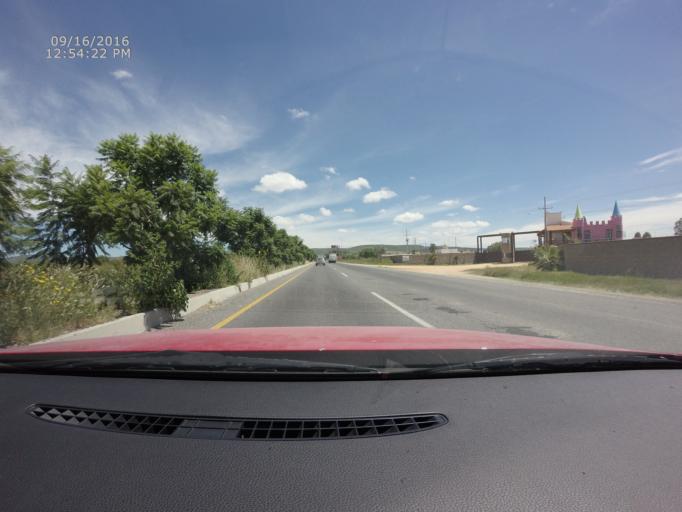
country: MX
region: Queretaro
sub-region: Colon
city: Purisima de Cubos (La Purisima)
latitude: 20.6313
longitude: -100.1200
